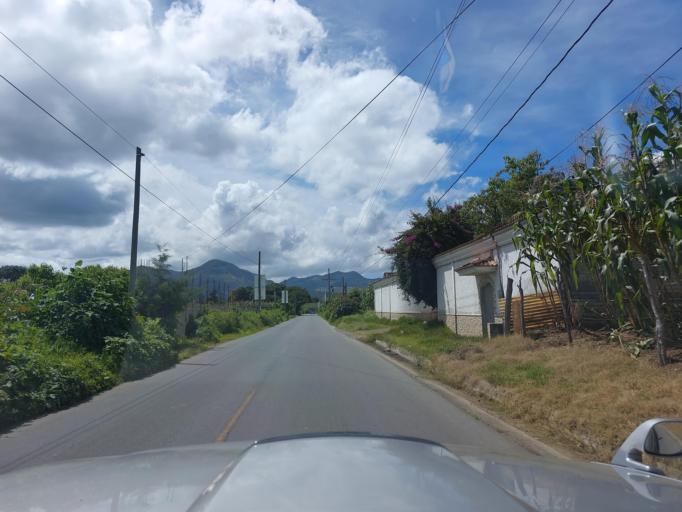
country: GT
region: Chimaltenango
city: Parramos
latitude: 14.6124
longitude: -90.8186
